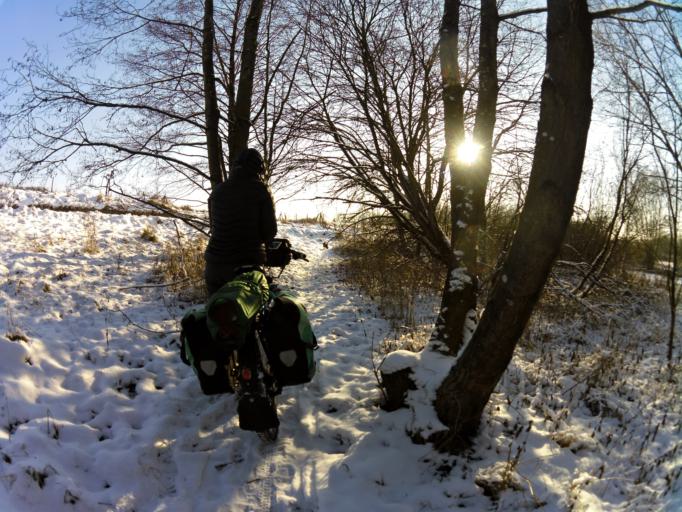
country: PL
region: West Pomeranian Voivodeship
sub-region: Powiat stargardzki
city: Dobrzany
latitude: 53.3507
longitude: 15.4206
